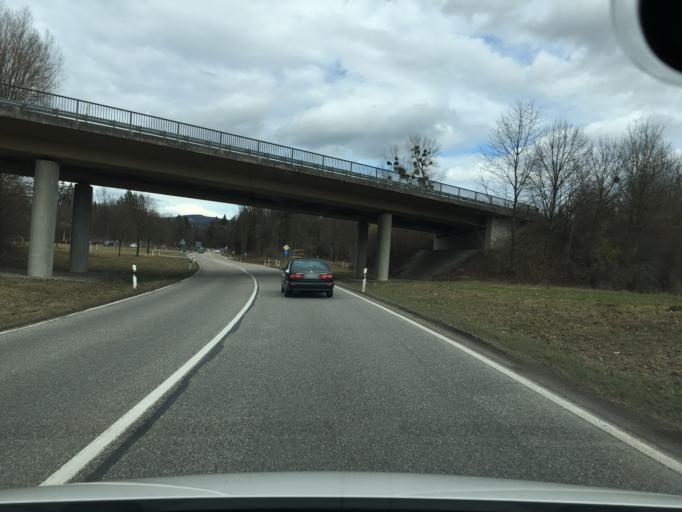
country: DE
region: Bavaria
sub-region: Upper Bavaria
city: Piding
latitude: 47.7443
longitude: 12.9071
